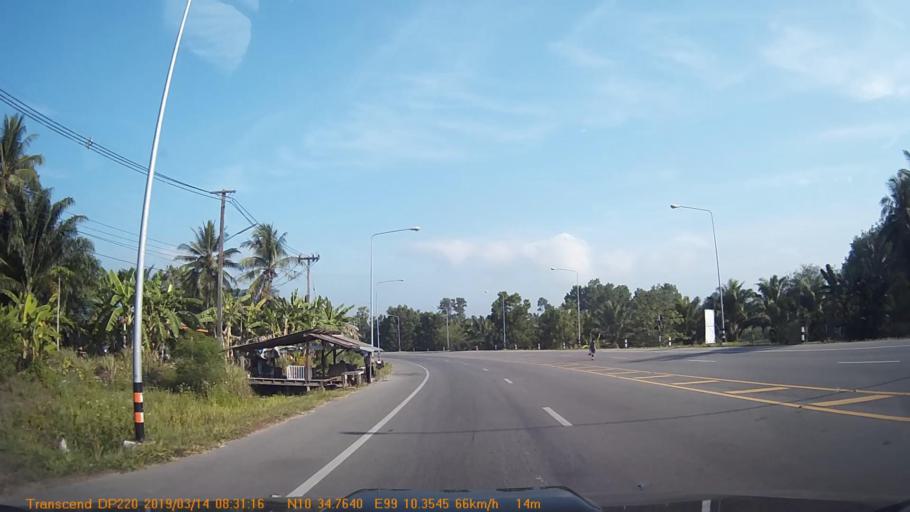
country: TH
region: Chumphon
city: Chumphon
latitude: 10.5794
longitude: 99.1726
